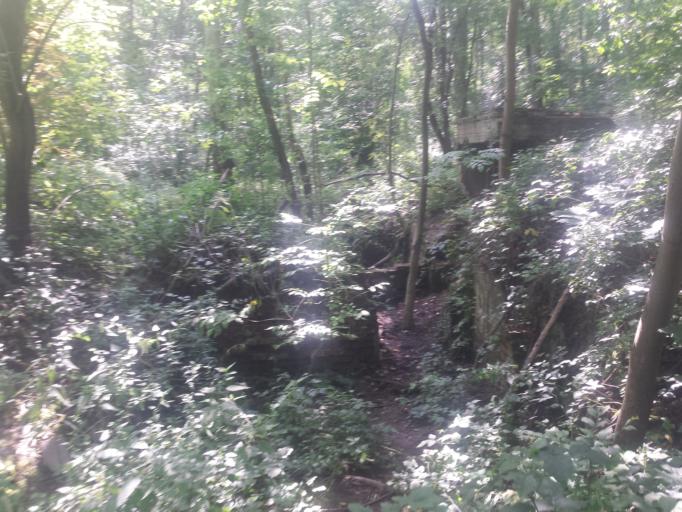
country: DE
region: Saxony
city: Taucha
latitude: 51.3910
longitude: 12.4762
